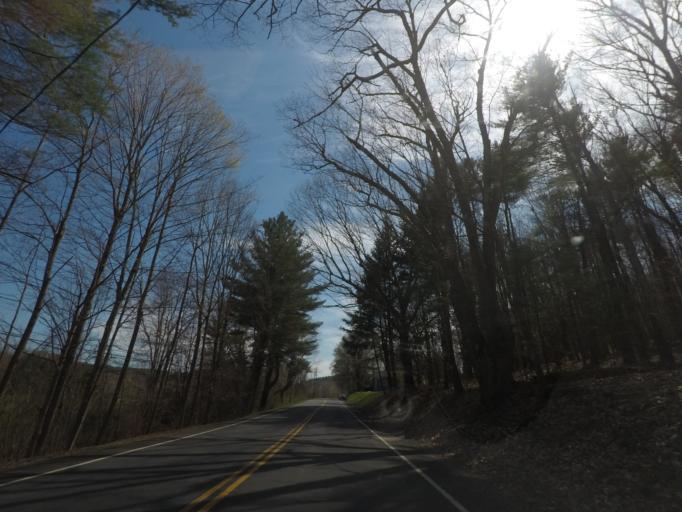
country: US
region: New York
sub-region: Columbia County
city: Chatham
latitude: 42.3890
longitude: -73.5302
